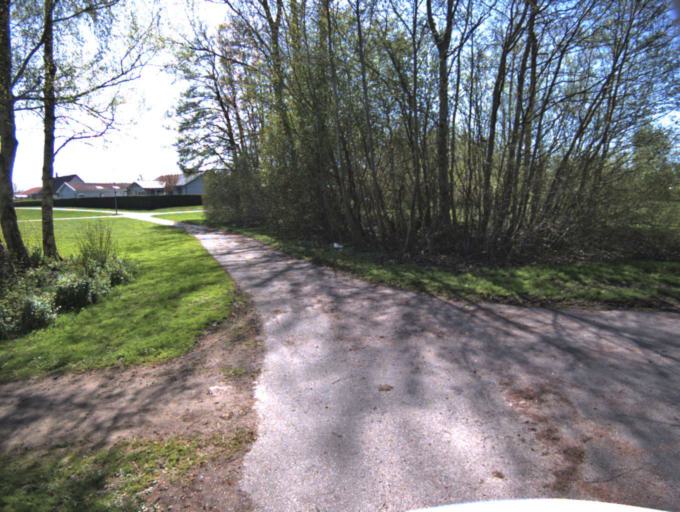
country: SE
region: Skane
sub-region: Kristianstads Kommun
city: Onnestad
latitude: 55.9987
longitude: 14.0726
